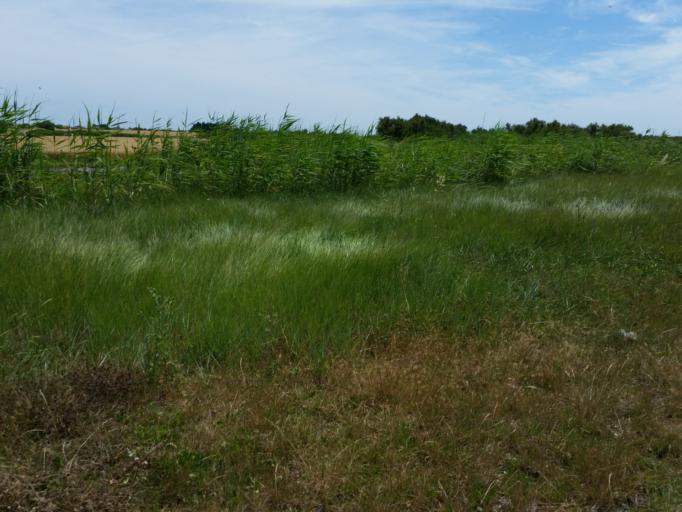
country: FR
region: Poitou-Charentes
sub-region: Departement de la Charente-Maritime
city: Port-des-Barques
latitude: 45.9213
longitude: -1.0738
